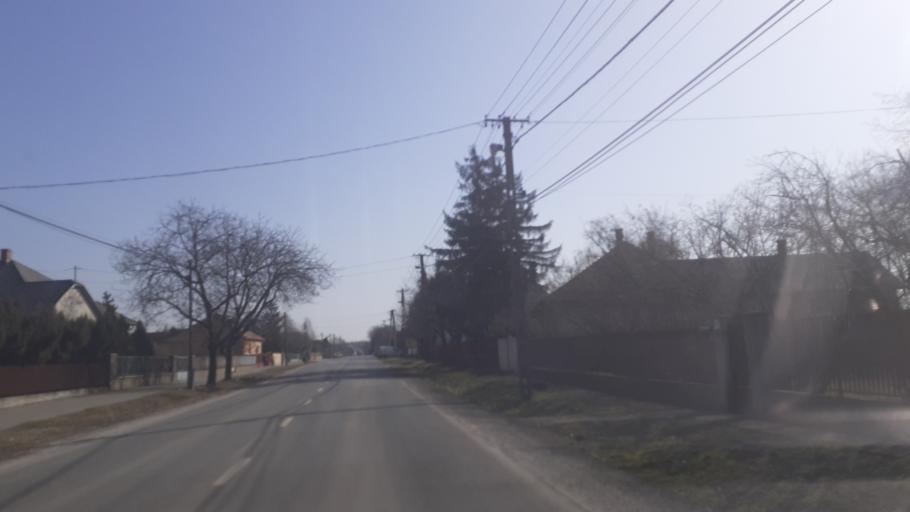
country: HU
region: Pest
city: Dabas
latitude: 47.1658
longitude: 19.3304
